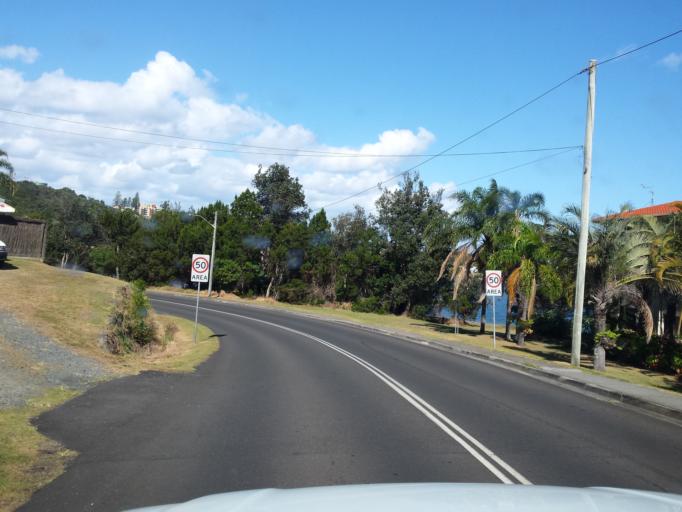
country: AU
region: New South Wales
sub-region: Ballina
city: East Ballina
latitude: -28.8660
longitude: 153.5808
